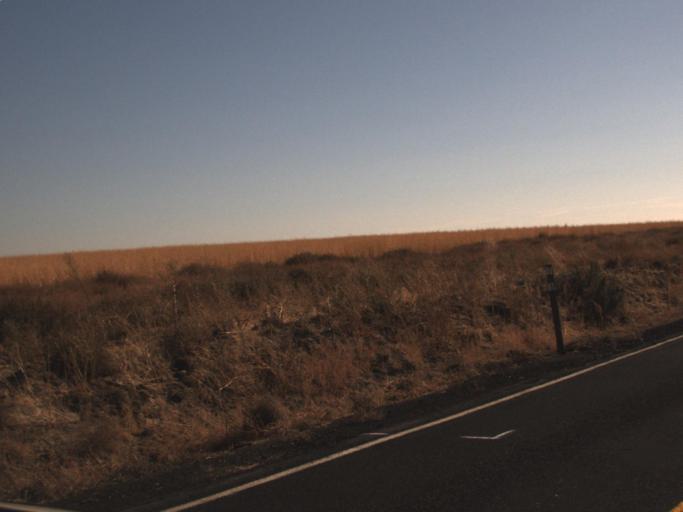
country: US
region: Washington
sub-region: Adams County
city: Ritzville
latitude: 47.0120
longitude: -118.6637
